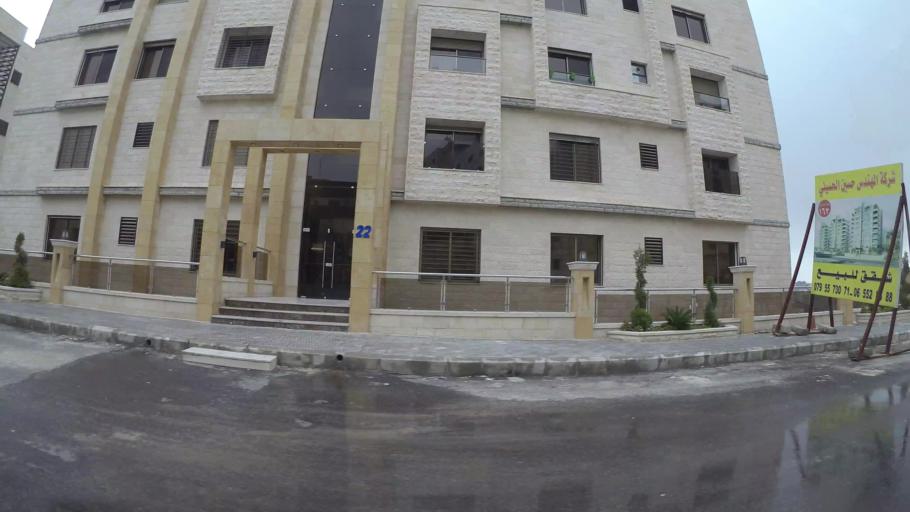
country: JO
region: Amman
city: Al Bunayyat ash Shamaliyah
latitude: 31.9373
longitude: 35.8699
